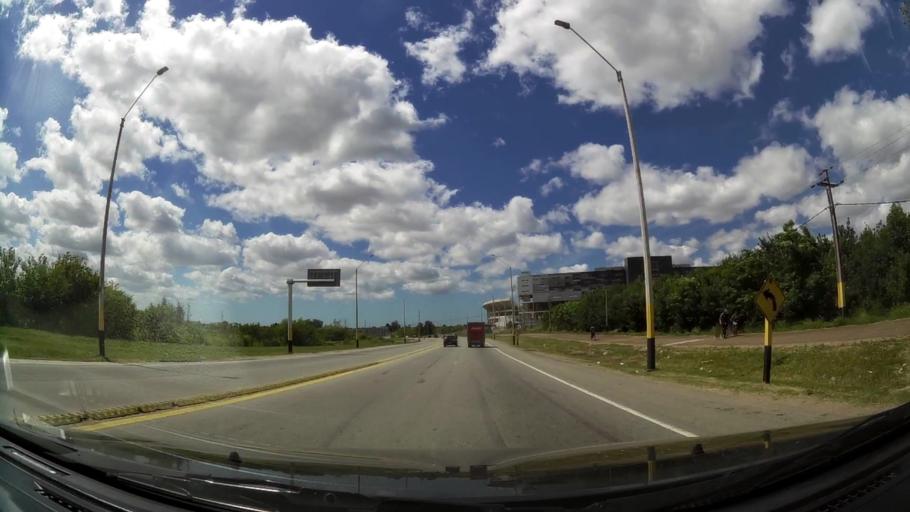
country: UY
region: Canelones
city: Colonia Nicolich
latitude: -34.7937
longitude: -56.0688
